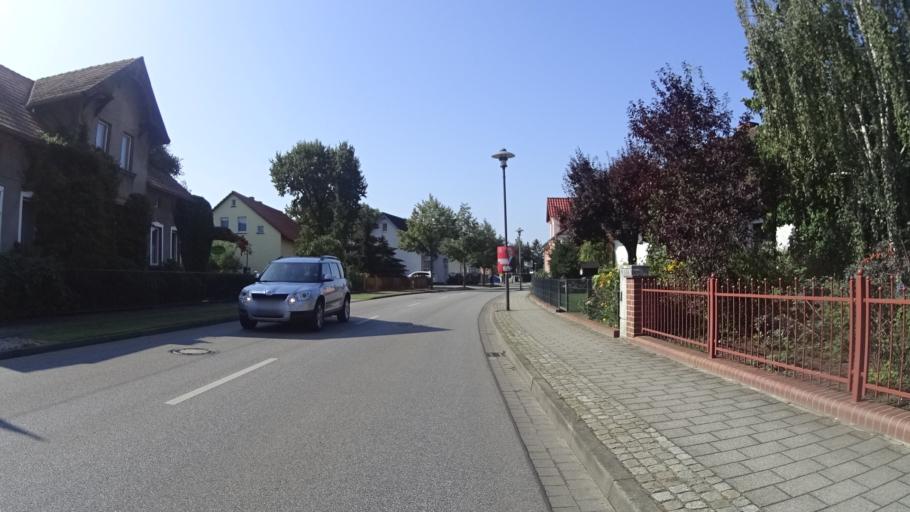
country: DE
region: Brandenburg
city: Burg
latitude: 51.8304
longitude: 14.1483
